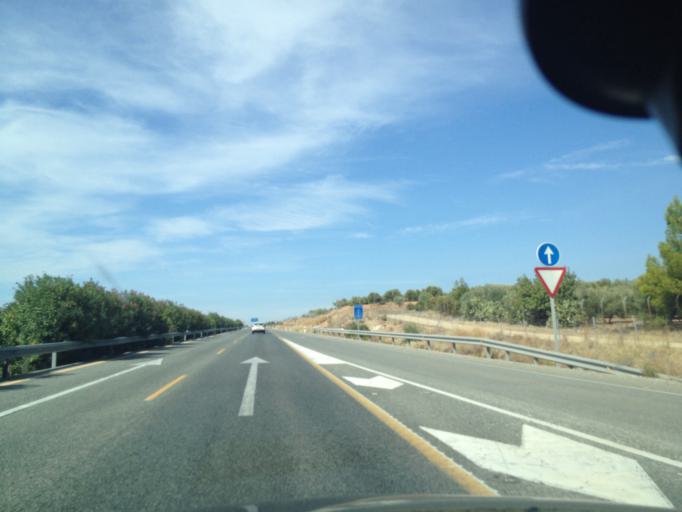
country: ES
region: Andalusia
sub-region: Provincia de Sevilla
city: La Puebla de Cazalla
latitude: 37.2324
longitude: -5.3034
